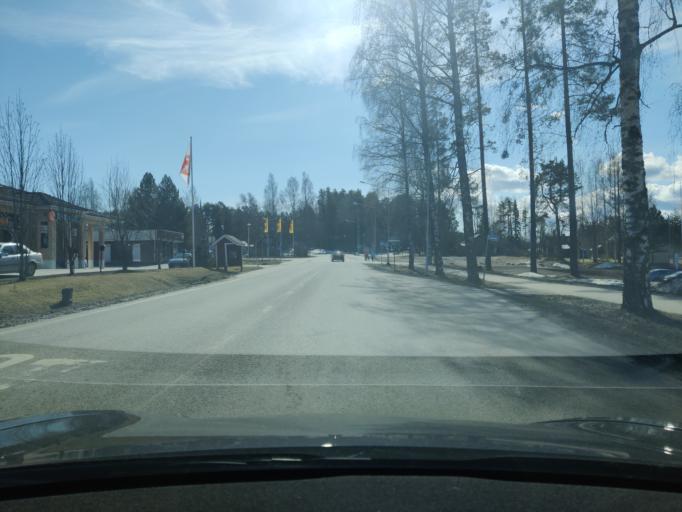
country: FI
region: Northern Savo
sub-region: Kuopio
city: Vehmersalmi
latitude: 62.7618
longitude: 28.0275
